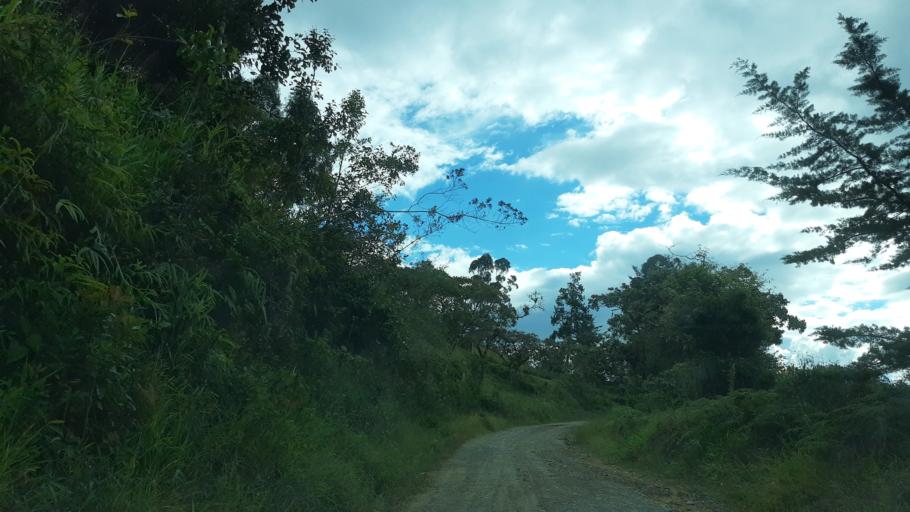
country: CO
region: Boyaca
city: Garagoa
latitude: 5.0153
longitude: -73.3357
